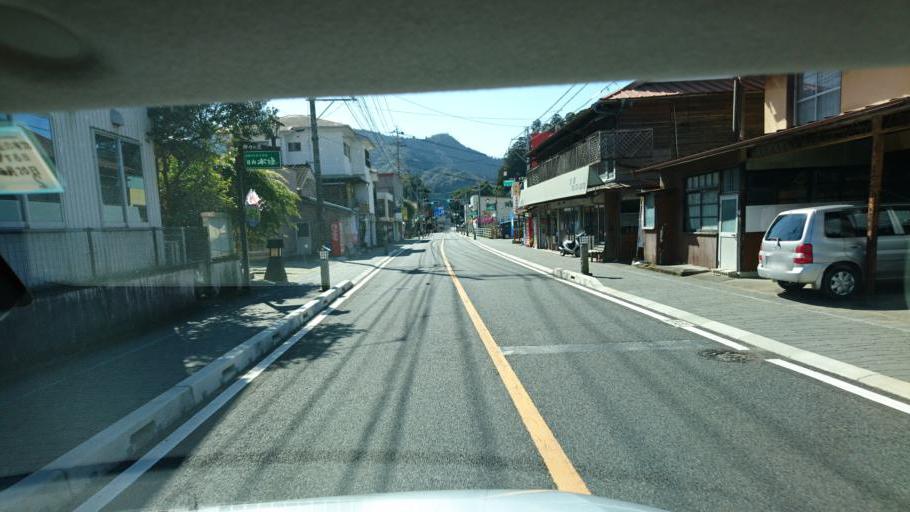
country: JP
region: Oita
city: Takedamachi
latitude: 32.7081
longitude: 131.3049
